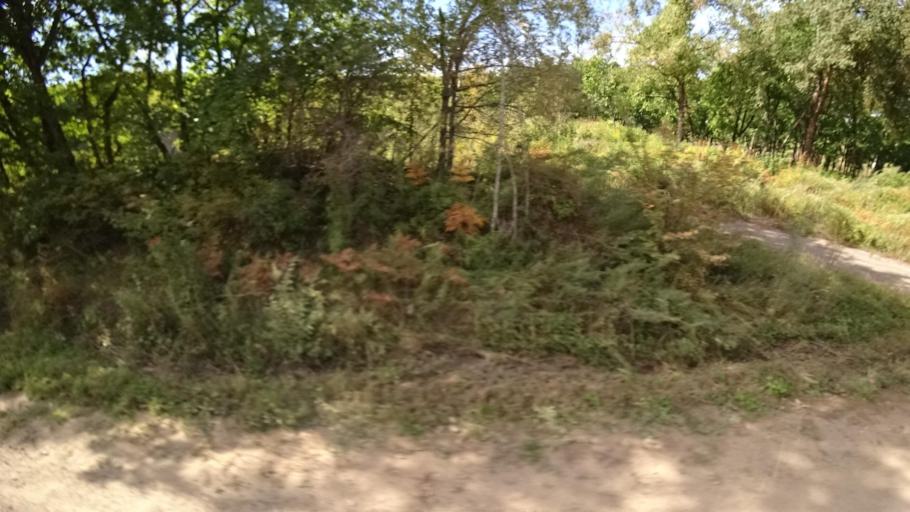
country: RU
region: Primorskiy
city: Yakovlevka
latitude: 44.3861
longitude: 133.5391
